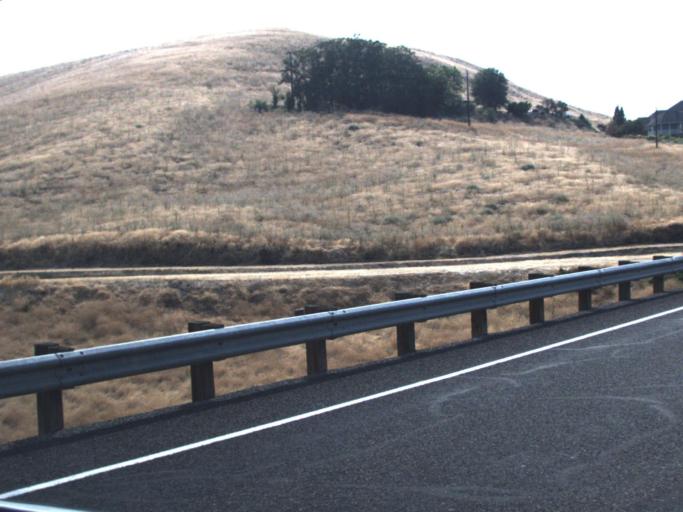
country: US
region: Washington
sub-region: Benton County
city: Prosser
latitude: 46.1956
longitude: -119.7819
